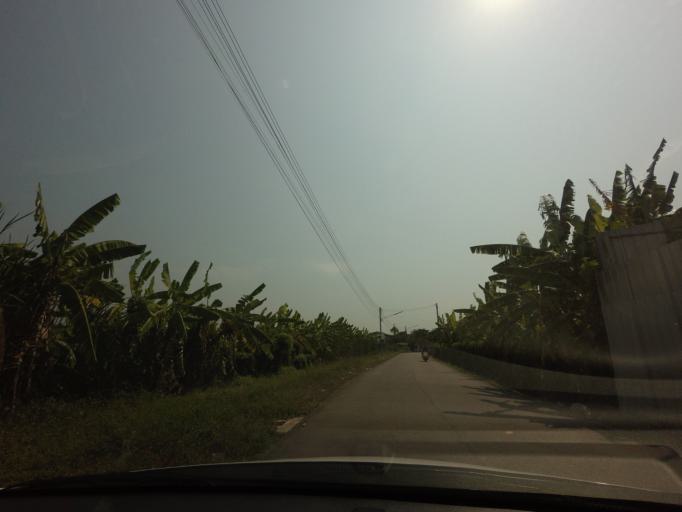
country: TH
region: Nakhon Pathom
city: Sam Phran
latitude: 13.7293
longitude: 100.2652
